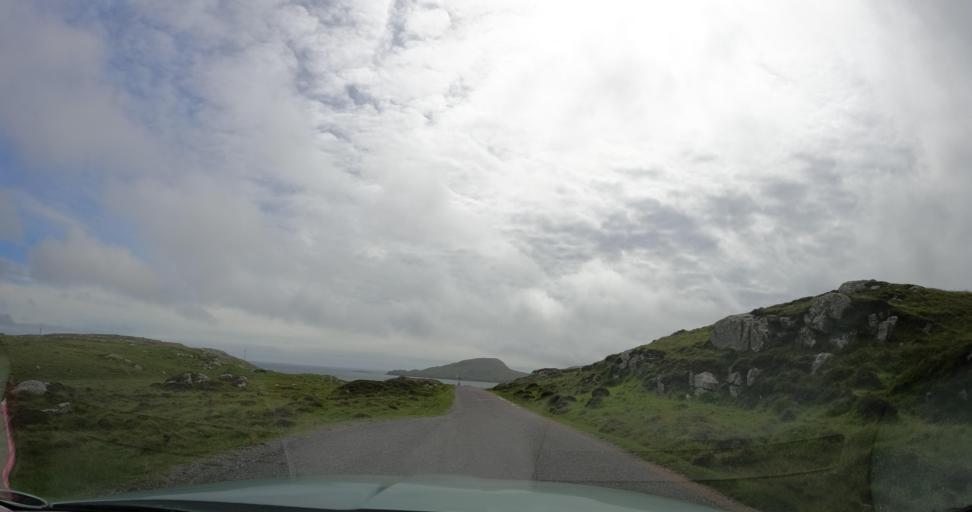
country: GB
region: Scotland
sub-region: Eilean Siar
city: Barra
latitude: 56.9355
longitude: -7.5192
